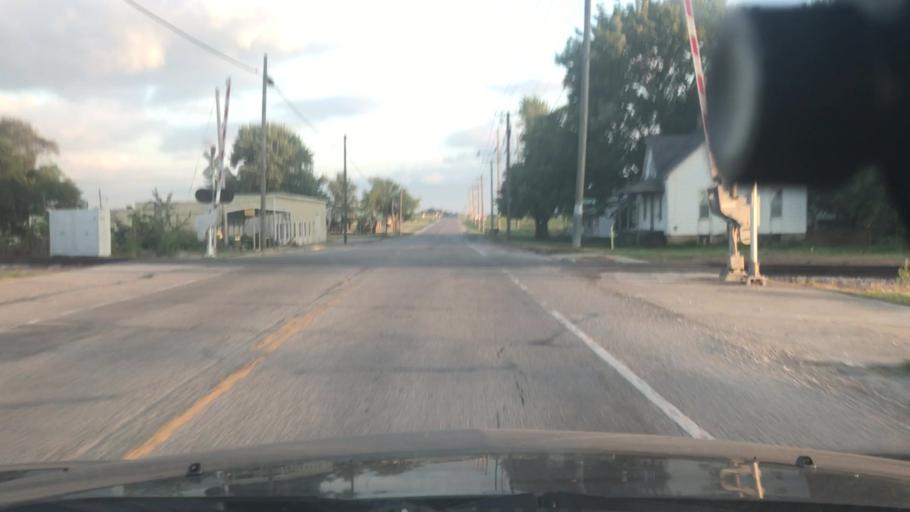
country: US
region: Illinois
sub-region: Washington County
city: Okawville
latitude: 38.4225
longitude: -89.5506
